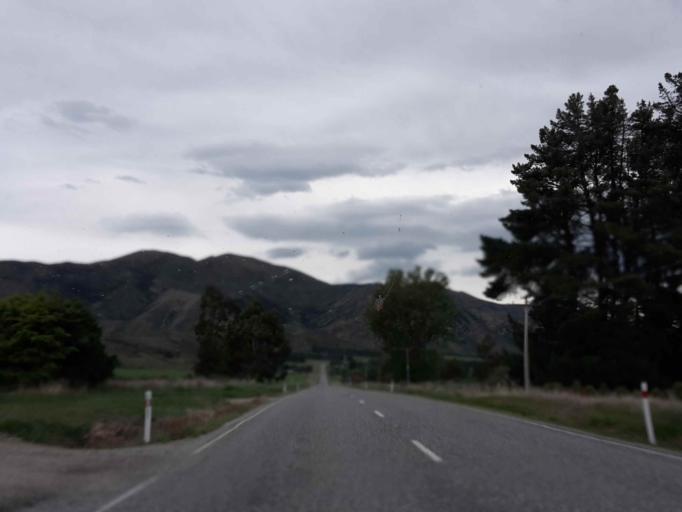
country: NZ
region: Otago
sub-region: Queenstown-Lakes District
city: Wanaka
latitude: -44.7358
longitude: 169.3196
